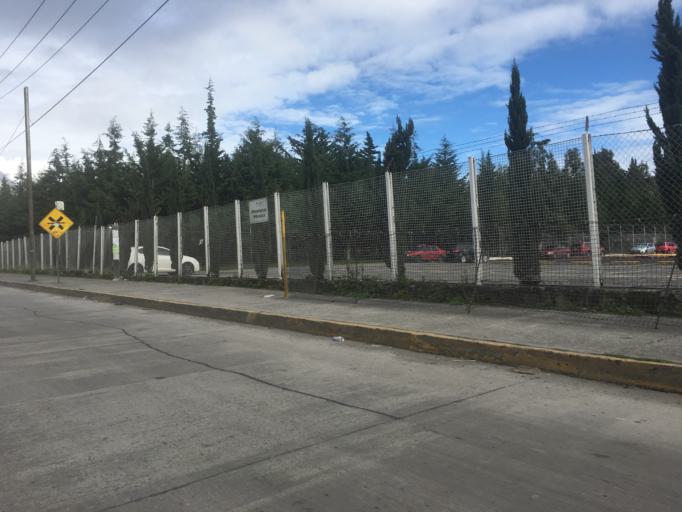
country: MX
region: Mexico
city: Santa Maria Totoltepec
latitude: 19.2881
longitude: -99.6069
